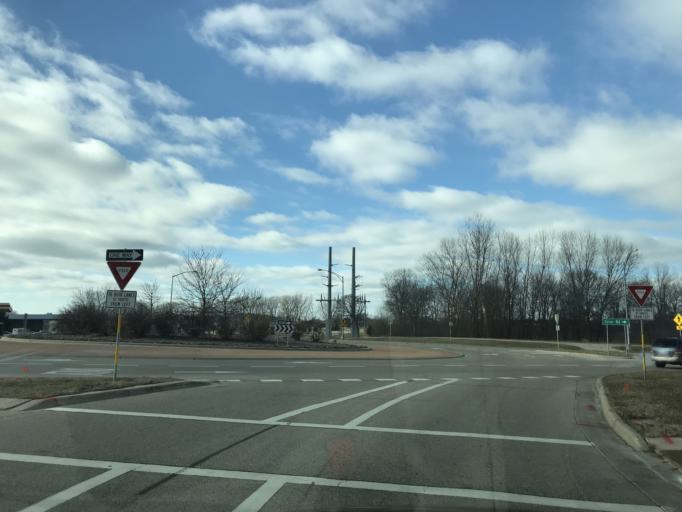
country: US
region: Wisconsin
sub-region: Dane County
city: Monona
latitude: 43.1215
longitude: -89.2987
